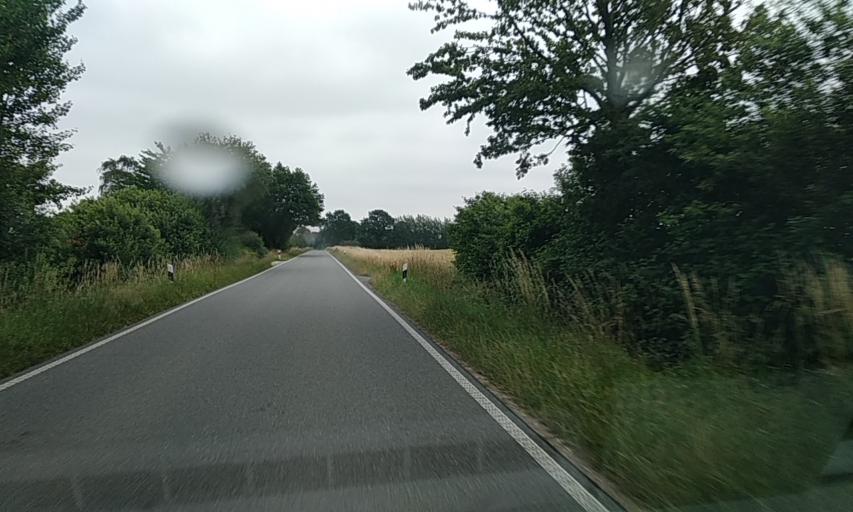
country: DE
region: Schleswig-Holstein
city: Steinfeld
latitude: 54.6046
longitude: 9.7260
